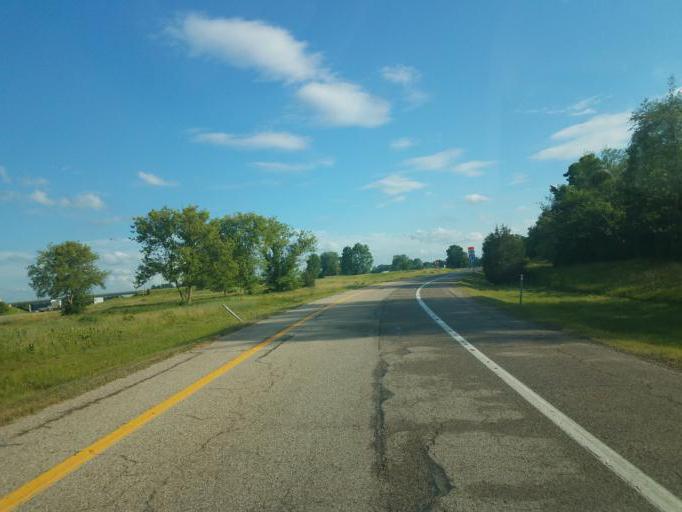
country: US
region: Indiana
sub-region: Steuben County
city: Fremont
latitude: 41.7999
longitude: -84.9966
